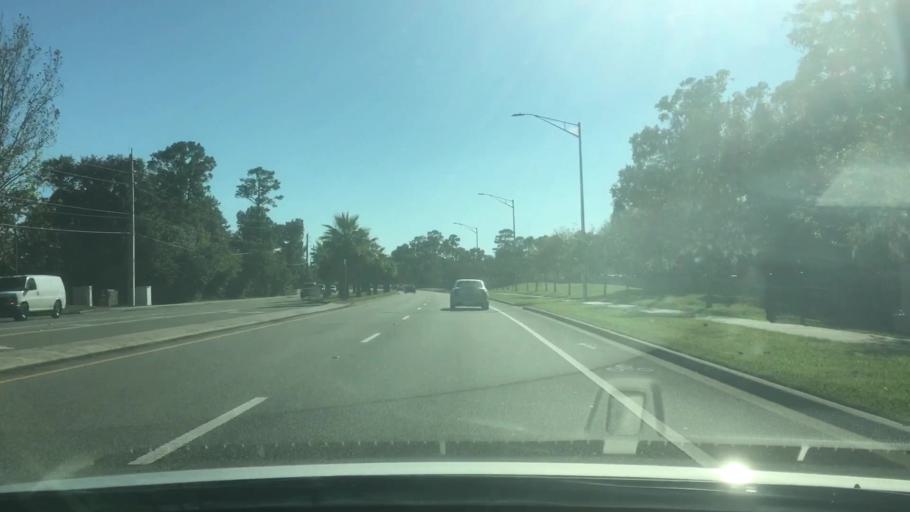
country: US
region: Florida
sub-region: Duval County
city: Neptune Beach
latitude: 30.3119
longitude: -81.4587
